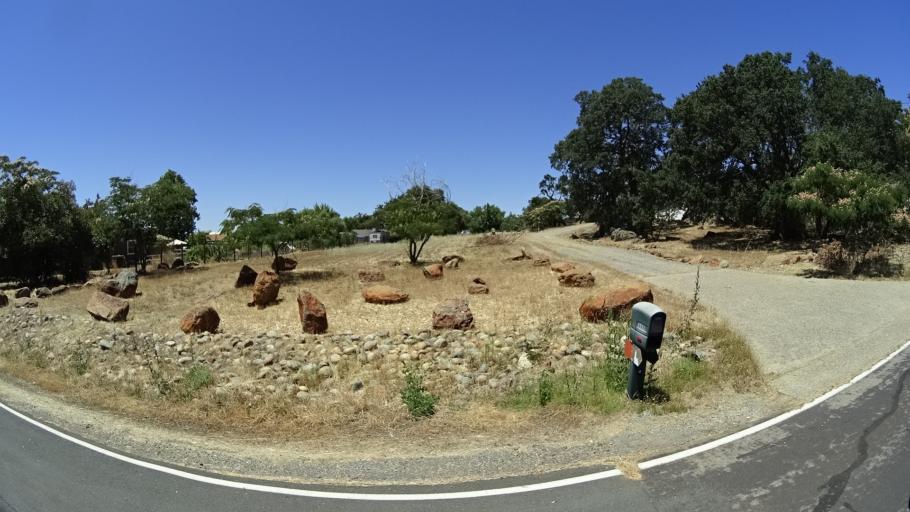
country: US
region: California
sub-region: Calaveras County
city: Rancho Calaveras
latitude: 38.1374
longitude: -120.8406
